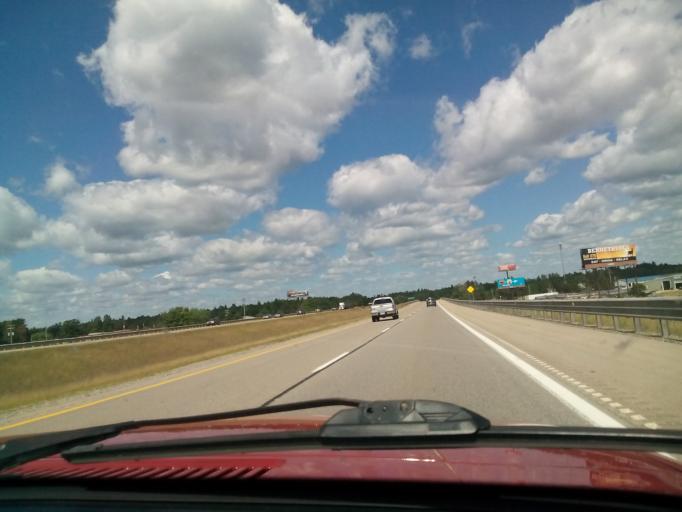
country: US
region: Michigan
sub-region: Crawford County
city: Grayling
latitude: 44.6536
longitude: -84.7018
